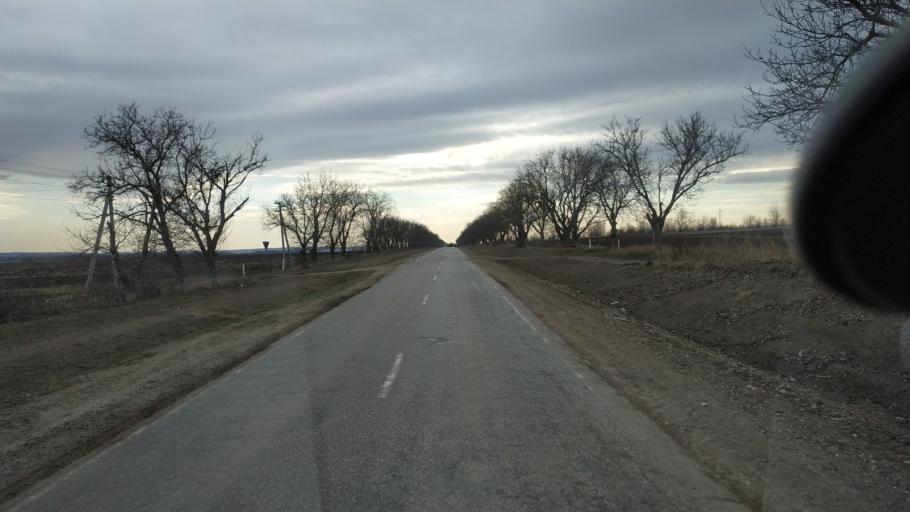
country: MD
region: Criuleni
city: Criuleni
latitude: 47.1860
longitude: 29.1416
